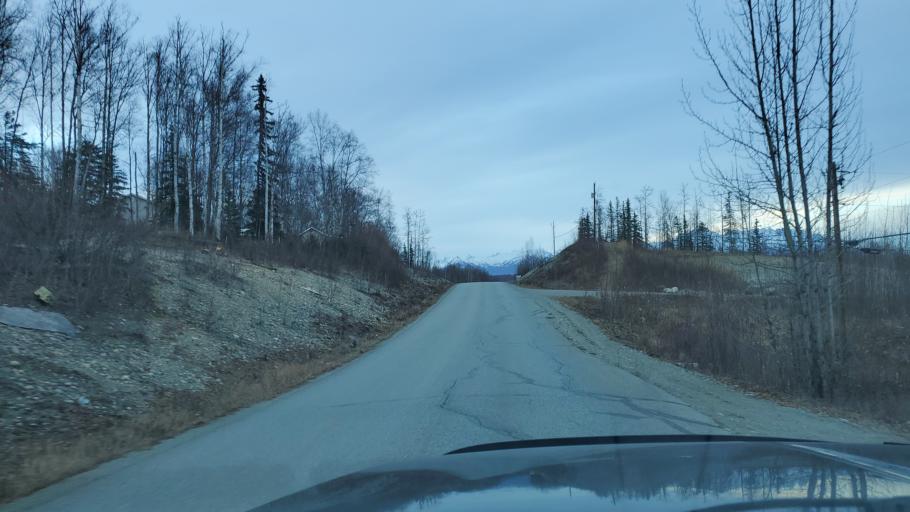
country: US
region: Alaska
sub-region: Matanuska-Susitna Borough
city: Lakes
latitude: 61.6572
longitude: -149.2927
